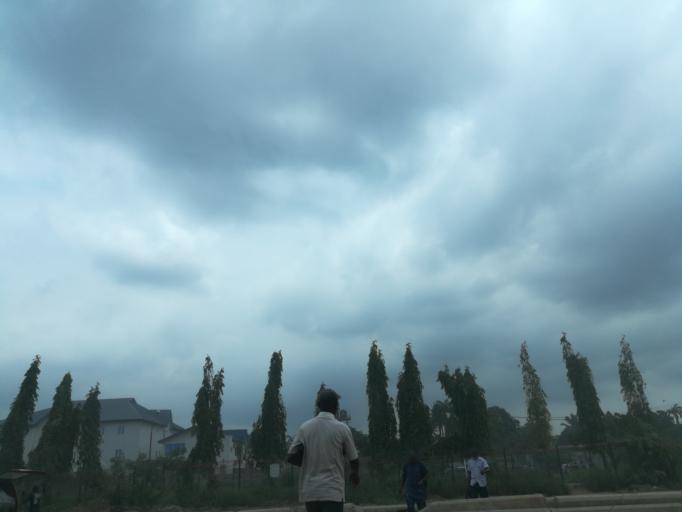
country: NG
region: Lagos
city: Oshodi
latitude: 6.5718
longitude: 3.3451
